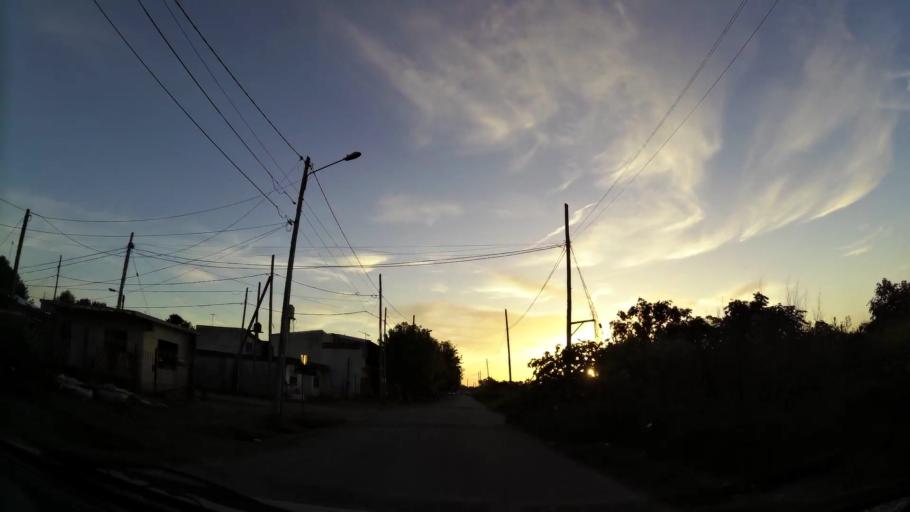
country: AR
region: Buenos Aires
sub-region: Partido de Quilmes
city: Quilmes
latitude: -34.7875
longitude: -58.2252
